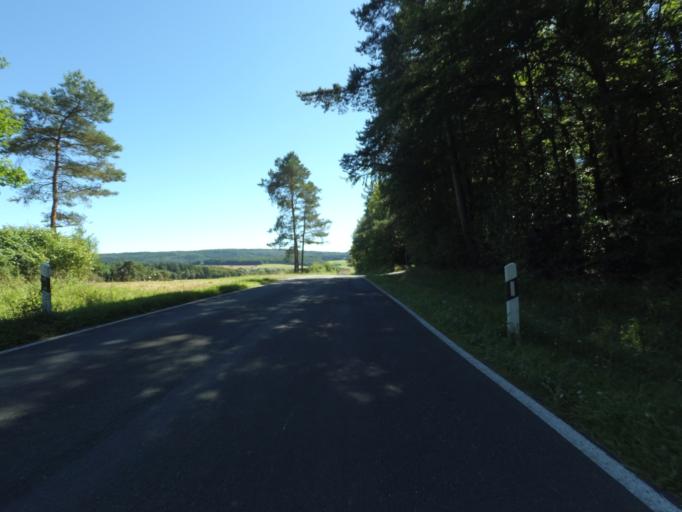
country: DE
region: Rheinland-Pfalz
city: Nohn
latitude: 50.3201
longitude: 6.7605
